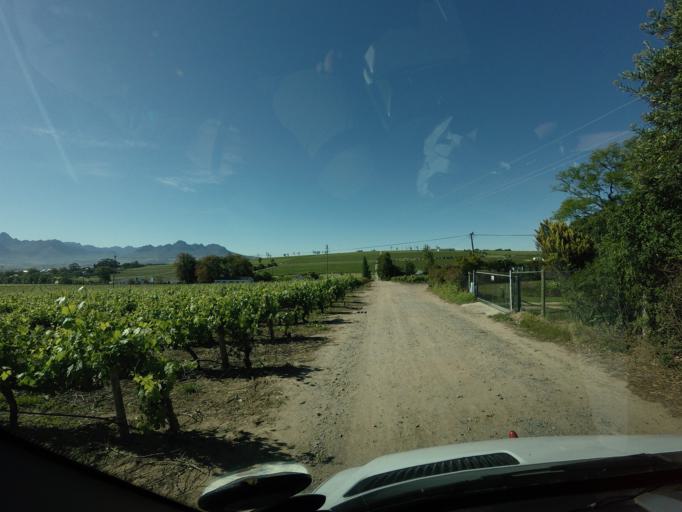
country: ZA
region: Western Cape
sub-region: Cape Winelands District Municipality
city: Stellenbosch
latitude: -33.9495
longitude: 18.7725
